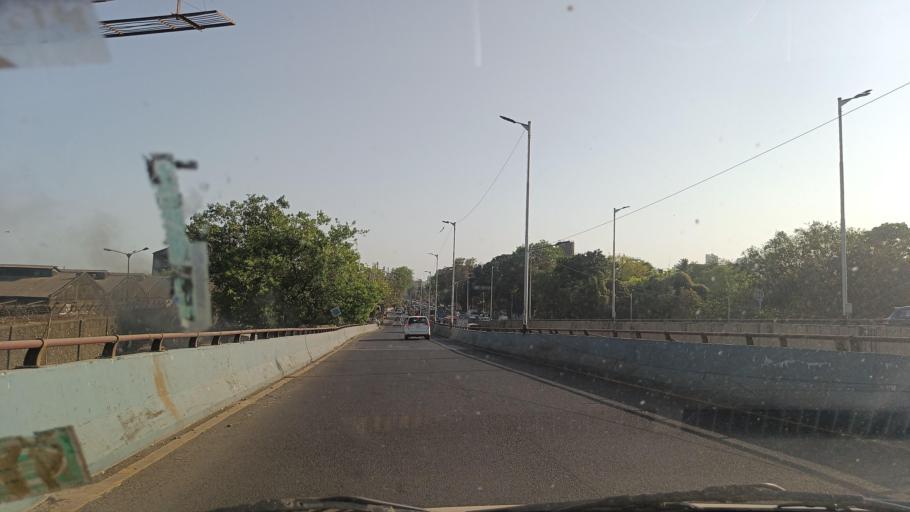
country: IN
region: Maharashtra
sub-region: Mumbai Suburban
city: Mumbai
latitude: 18.9590
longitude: 72.8434
